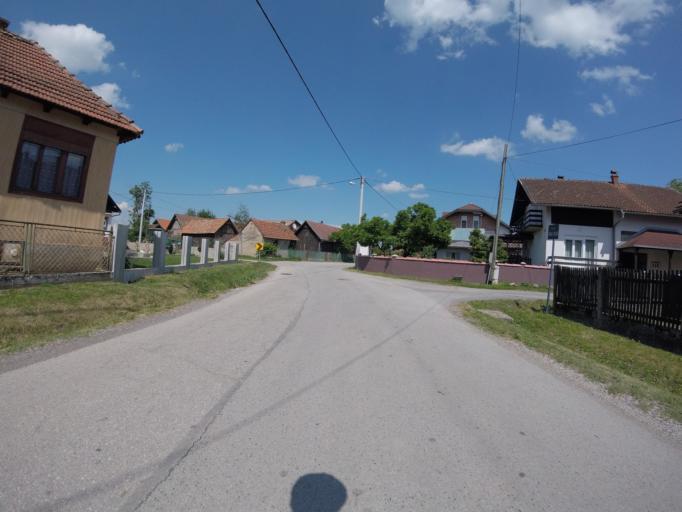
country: HR
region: Zagrebacka
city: Kuce
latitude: 45.6778
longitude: 16.1517
